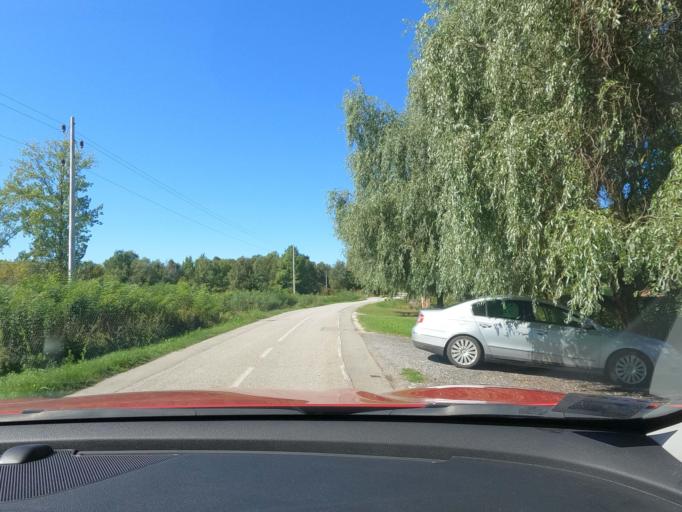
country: HR
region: Sisacko-Moslavacka
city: Petrinja
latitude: 45.4678
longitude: 16.3017
